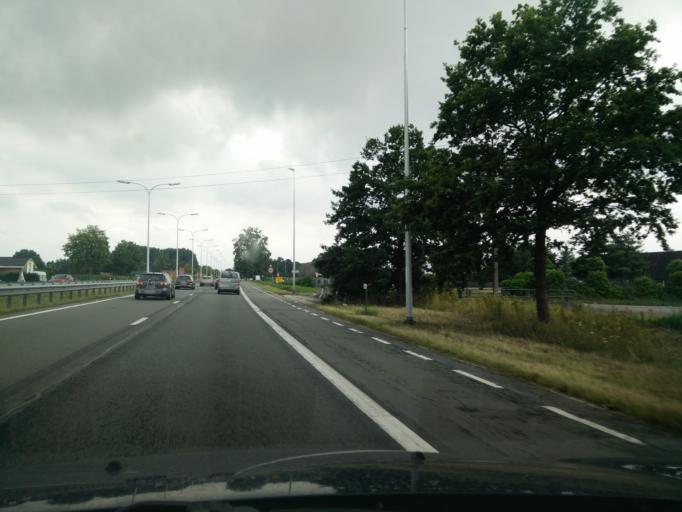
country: BE
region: Flanders
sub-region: Provincie Oost-Vlaanderen
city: Gavere
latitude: 50.9289
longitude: 3.6268
